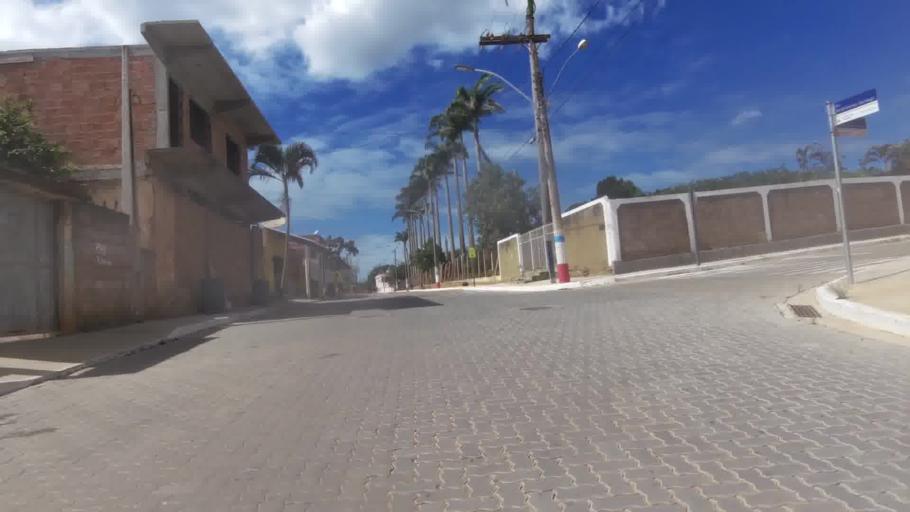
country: BR
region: Espirito Santo
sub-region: Marataizes
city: Marataizes
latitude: -21.1807
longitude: -40.9856
